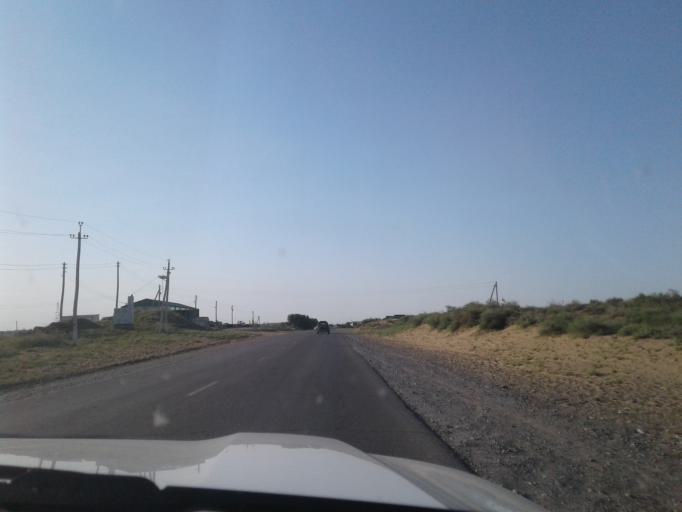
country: TM
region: Mary
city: Yoloeten
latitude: 37.2680
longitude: 62.3608
